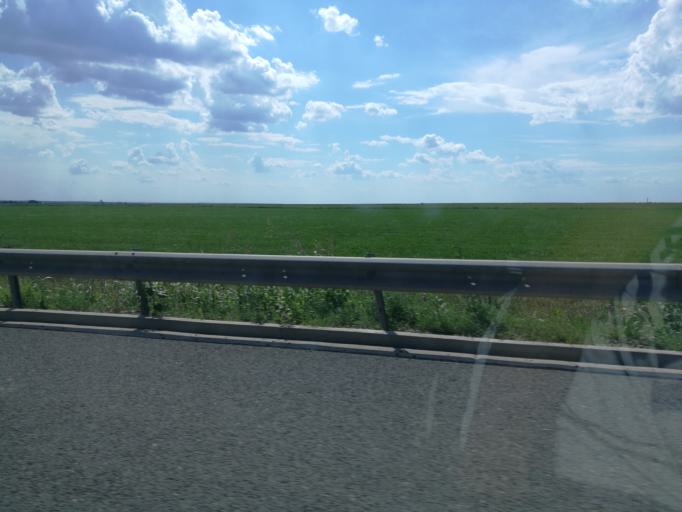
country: RO
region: Constanta
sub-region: Municipiul Constanta
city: Palazu Mare
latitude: 44.1861
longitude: 28.5506
